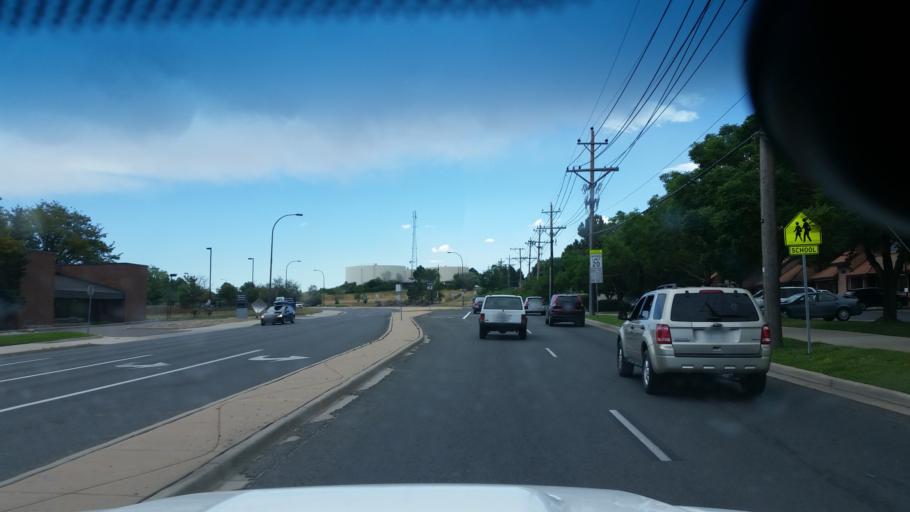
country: US
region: Colorado
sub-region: Adams County
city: Northglenn
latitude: 39.8997
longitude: -104.9964
